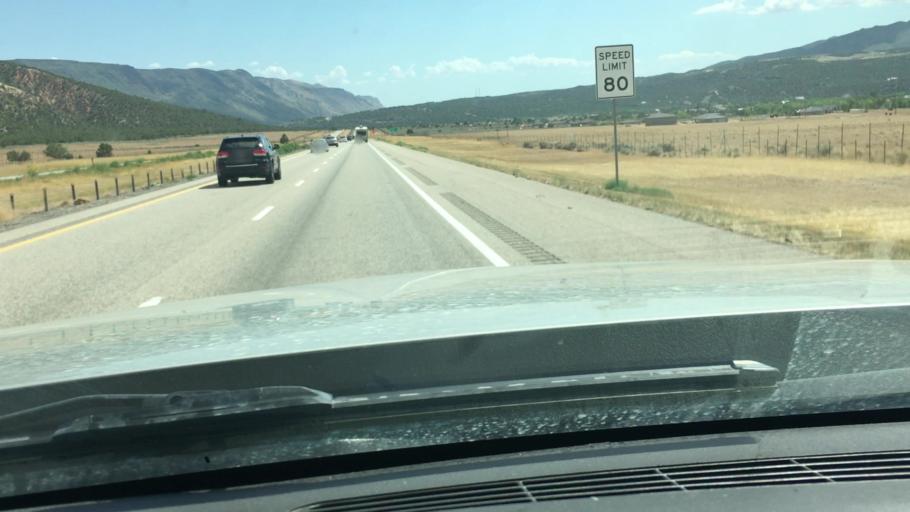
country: US
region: Utah
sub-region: Washington County
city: Toquerville
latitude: 37.4443
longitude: -113.2311
